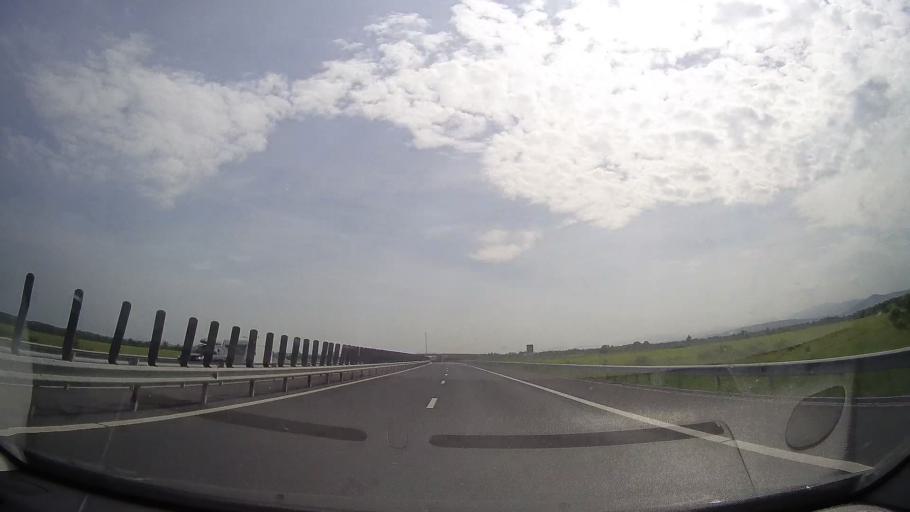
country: RO
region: Timis
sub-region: Comuna Manastiur
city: Manastiur
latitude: 45.8152
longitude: 22.0091
